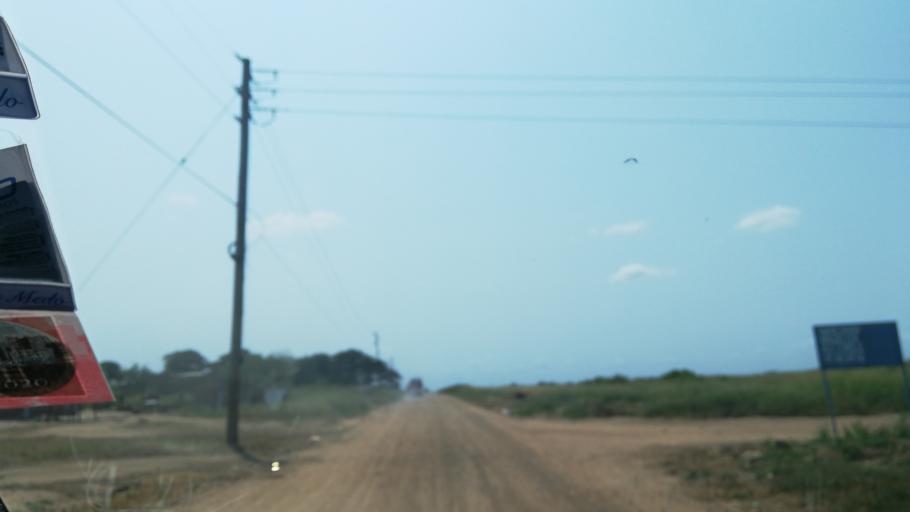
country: MZ
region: Maputo
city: Matola
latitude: -26.0662
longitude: 32.3902
